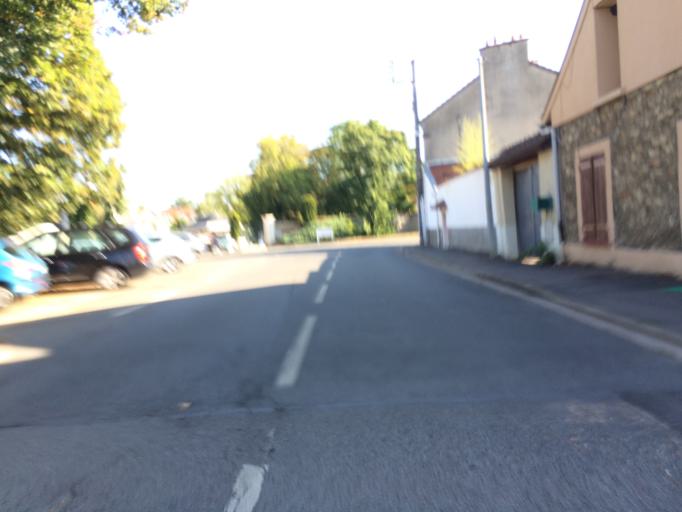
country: FR
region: Ile-de-France
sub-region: Departement de l'Essonne
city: Villiers-sur-Orge
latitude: 48.6621
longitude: 2.3078
